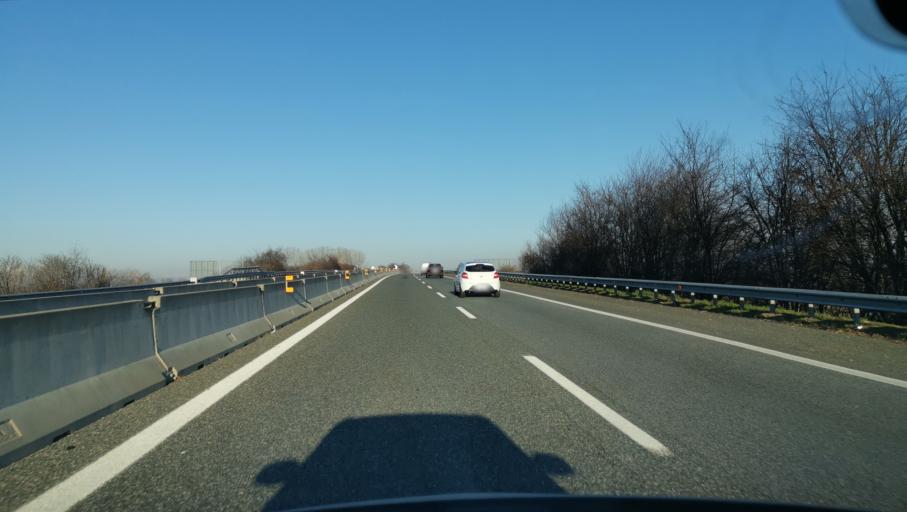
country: IT
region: Piedmont
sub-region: Provincia di Torino
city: Airasca
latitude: 44.9225
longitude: 7.4555
